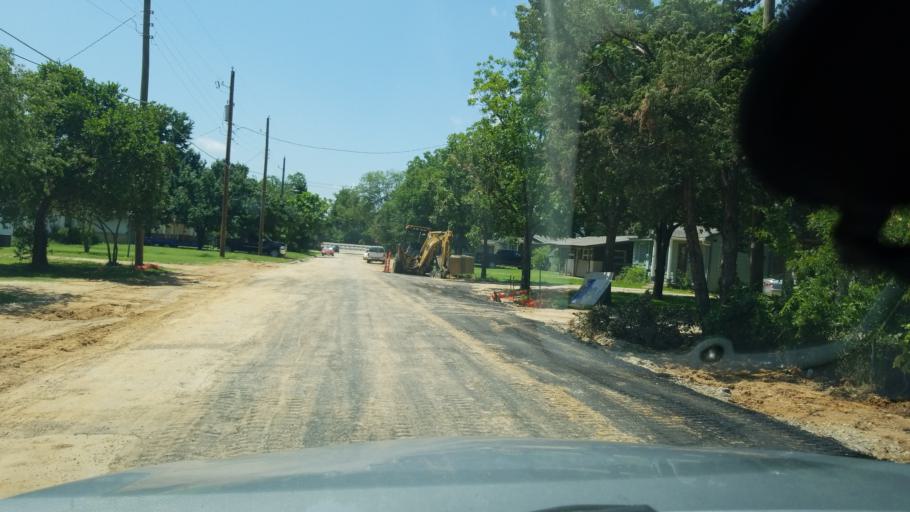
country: US
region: Texas
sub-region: Dallas County
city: Irving
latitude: 32.8191
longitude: -96.9622
